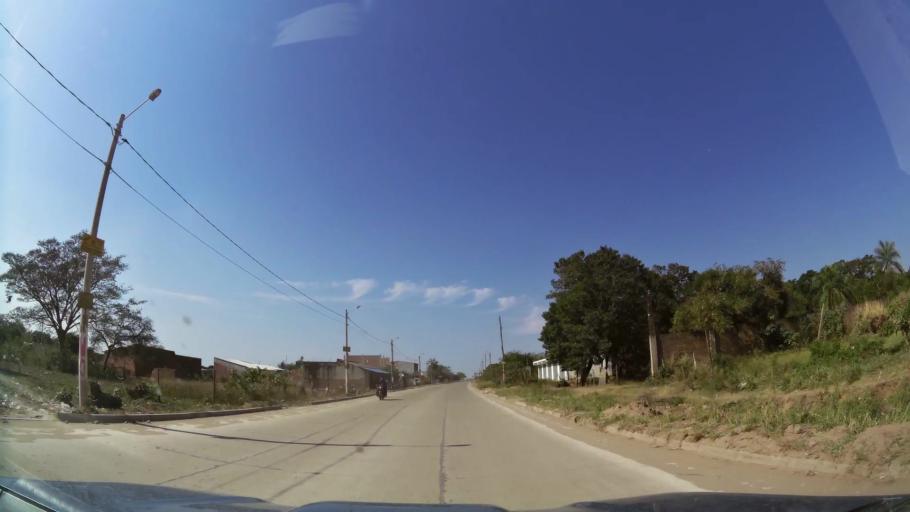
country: BO
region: Santa Cruz
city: Cotoca
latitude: -17.7257
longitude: -63.0852
